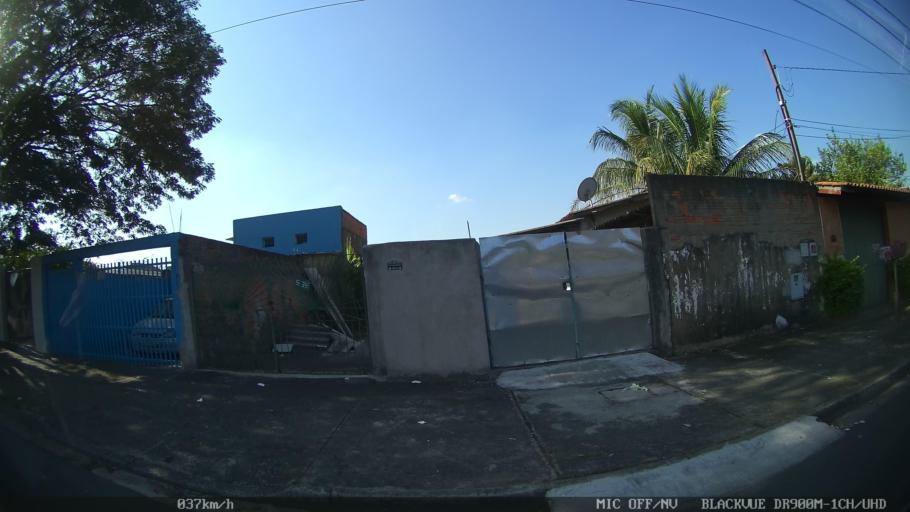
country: BR
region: Sao Paulo
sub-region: Indaiatuba
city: Indaiatuba
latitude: -22.9972
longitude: -47.1398
